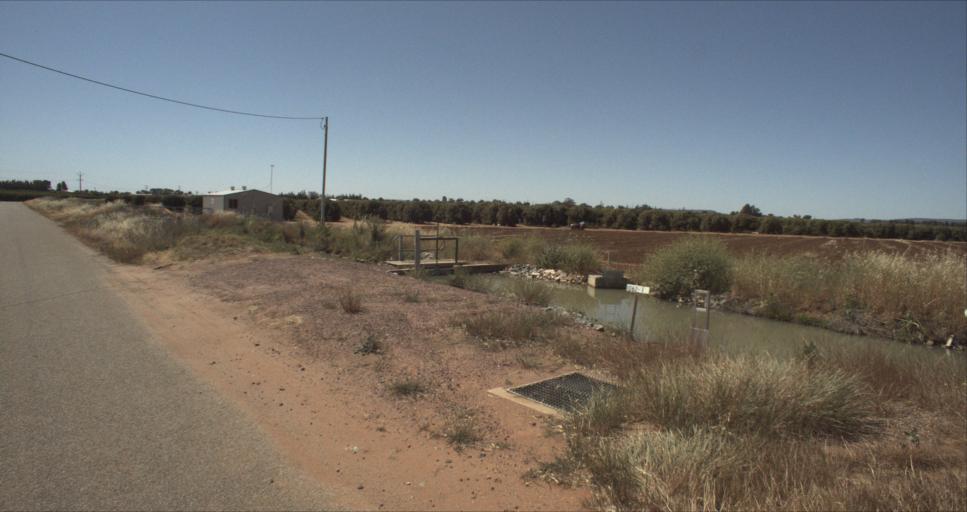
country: AU
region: New South Wales
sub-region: Leeton
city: Leeton
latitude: -34.5404
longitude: 146.3524
